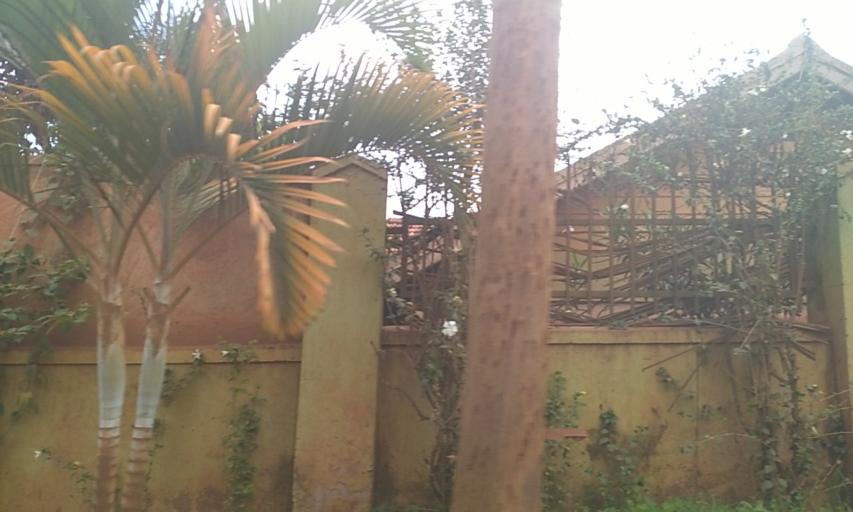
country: UG
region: Central Region
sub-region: Wakiso District
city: Kireka
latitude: 0.3439
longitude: 32.6213
